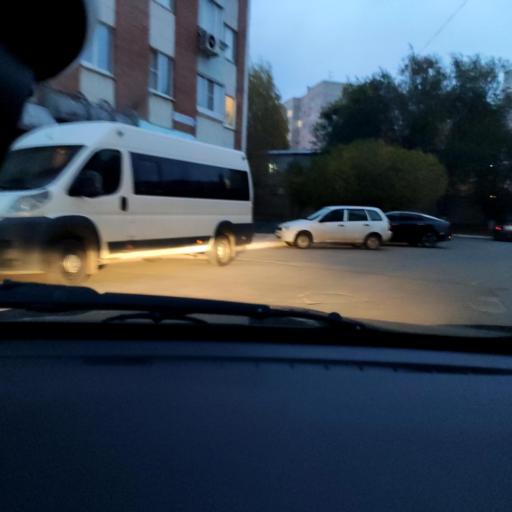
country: RU
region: Samara
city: Tol'yatti
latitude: 53.5442
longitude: 49.3389
